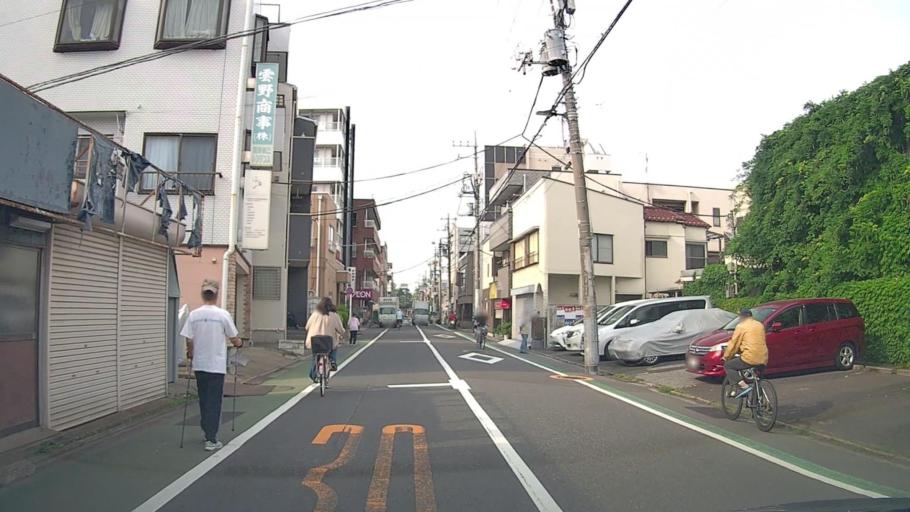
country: JP
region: Saitama
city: Soka
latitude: 35.7540
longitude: 139.7982
